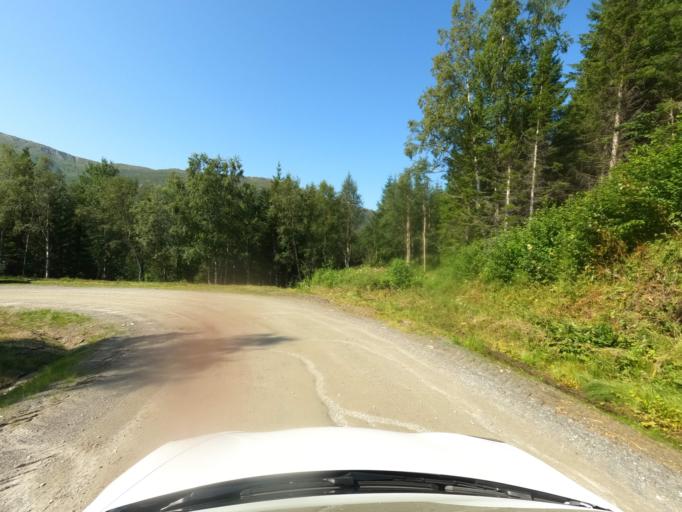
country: NO
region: Nordland
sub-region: Ballangen
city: Ballangen
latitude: 68.2625
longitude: 16.7133
